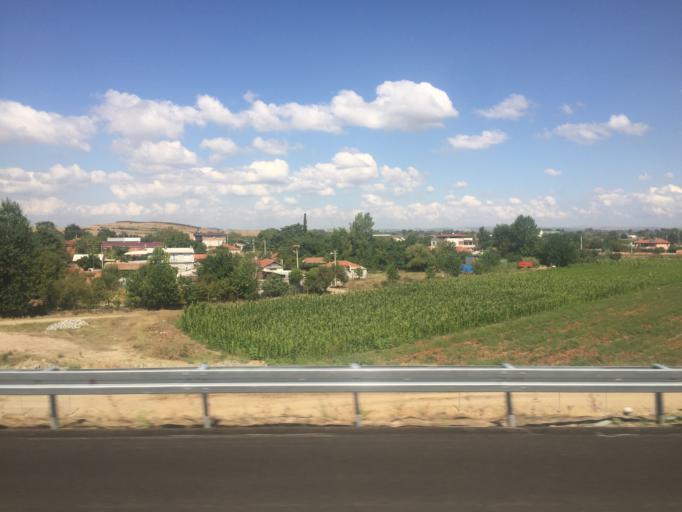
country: TR
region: Balikesir
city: Gobel
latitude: 40.0537
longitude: 28.2338
